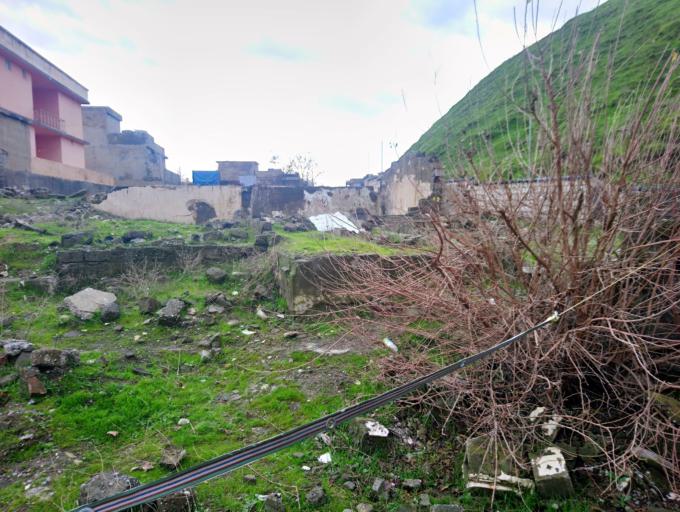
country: IQ
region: As Sulaymaniyah
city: Qeladize
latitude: 36.1862
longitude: 45.1154
